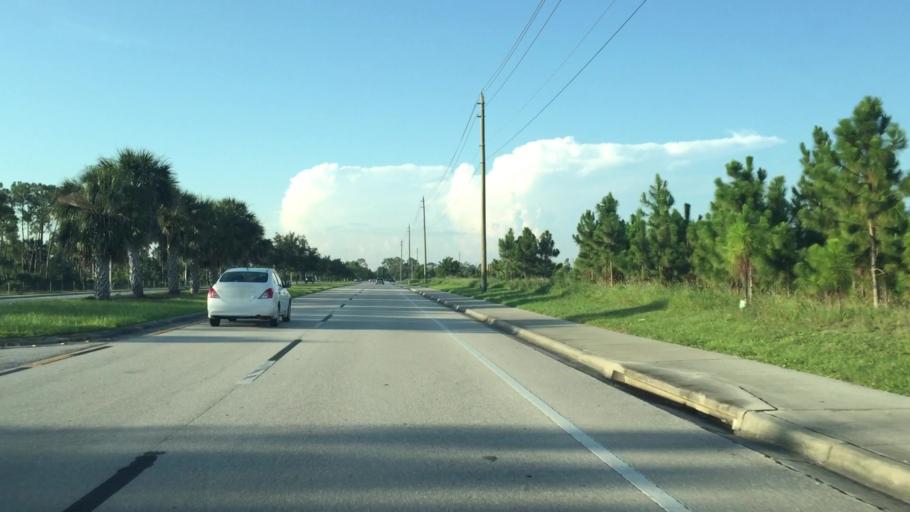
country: US
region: Florida
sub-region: Lee County
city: Three Oaks
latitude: 26.4618
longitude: -81.7888
